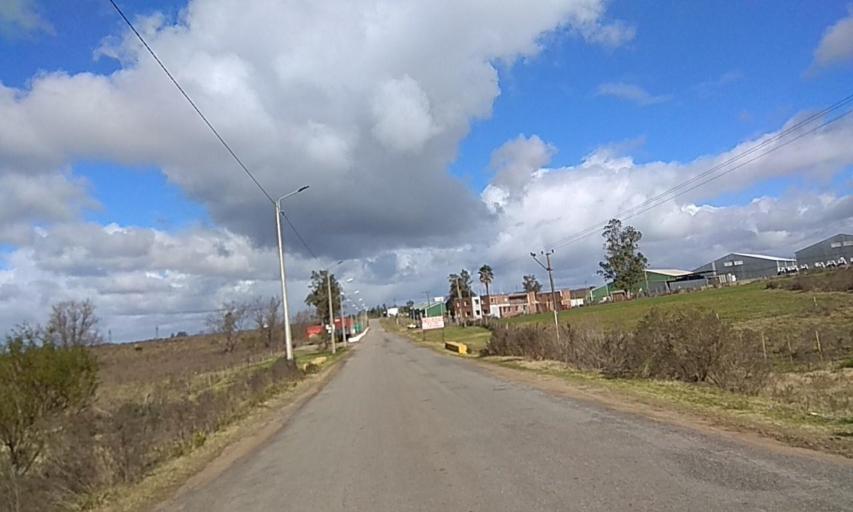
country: UY
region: Florida
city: Florida
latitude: -34.1108
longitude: -56.2261
